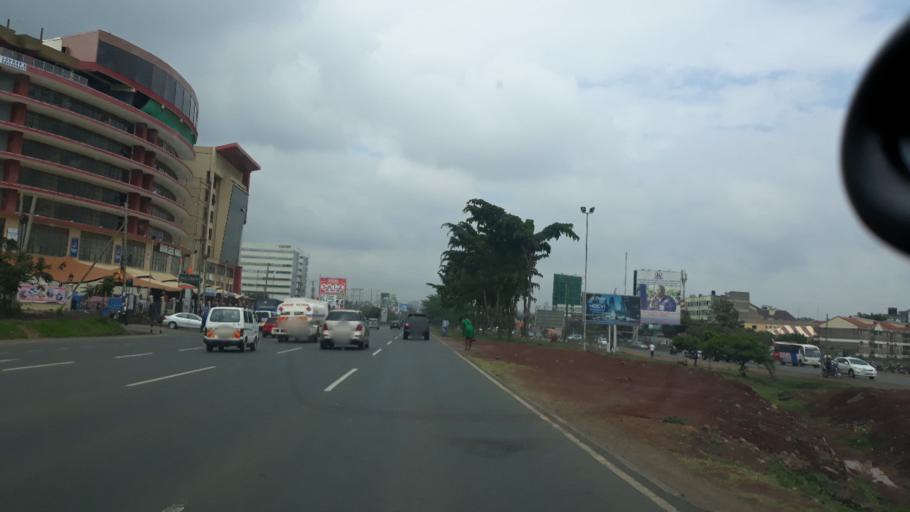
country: KE
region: Nairobi Area
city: Pumwani
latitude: -1.3238
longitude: 36.8451
